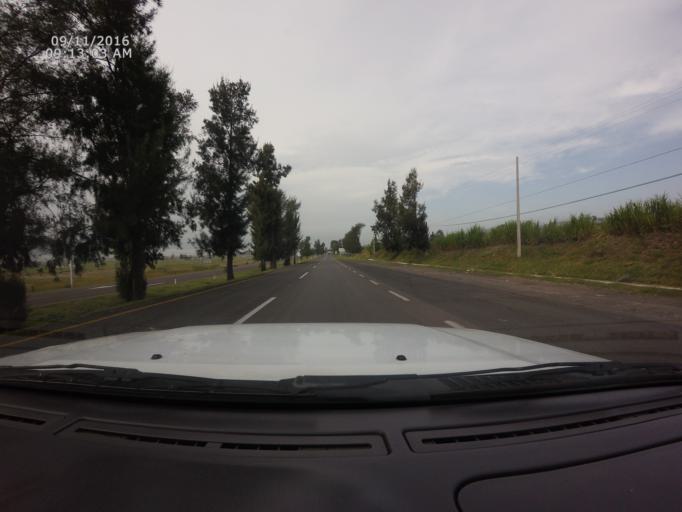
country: MX
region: Michoacan
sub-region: Morelia
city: La Mintzita (Piedra Dura)
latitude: 19.5861
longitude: -101.3044
